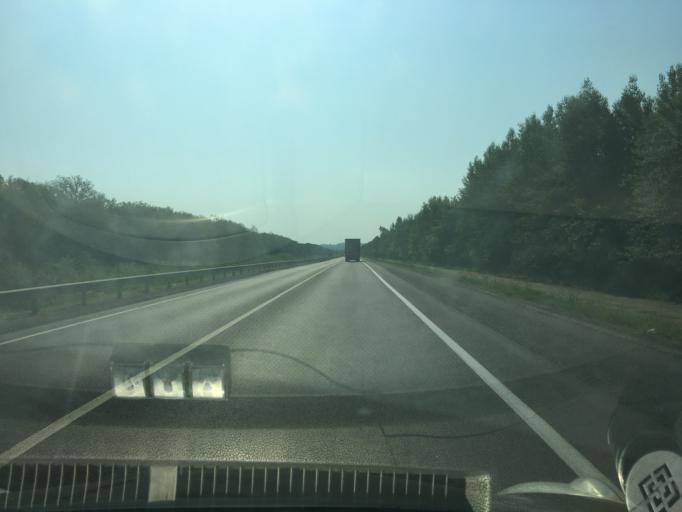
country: RU
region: Nizjnij Novgorod
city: Kstovo
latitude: 56.0874
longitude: 44.3409
